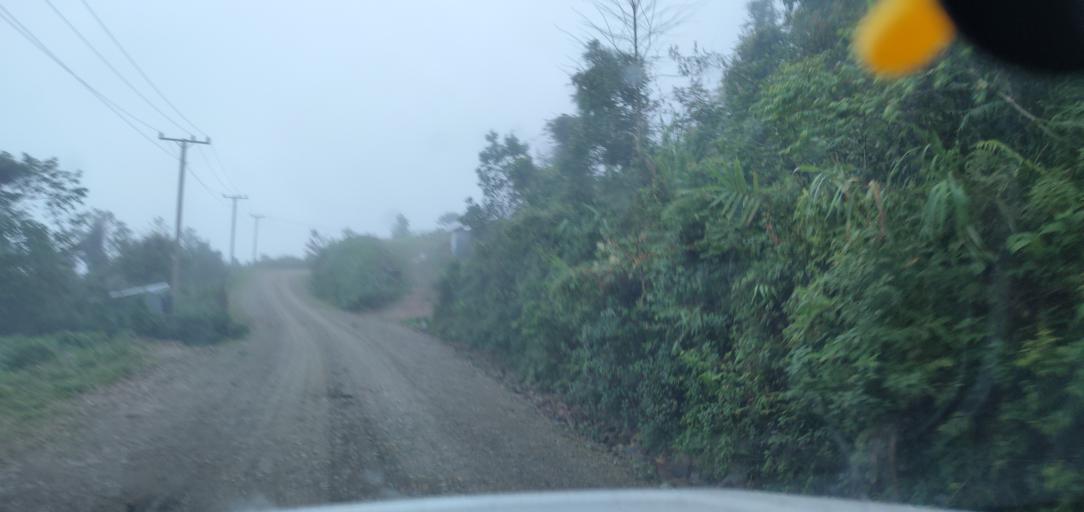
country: LA
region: Phongsali
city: Phongsali
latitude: 21.3902
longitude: 102.2006
